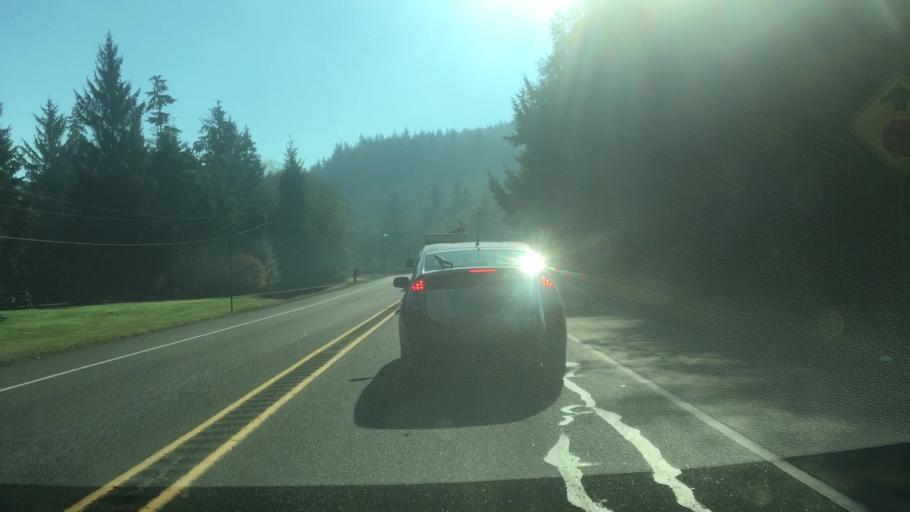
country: US
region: Washington
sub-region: Grays Harbor County
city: Central Park
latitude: 46.9197
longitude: -123.7184
